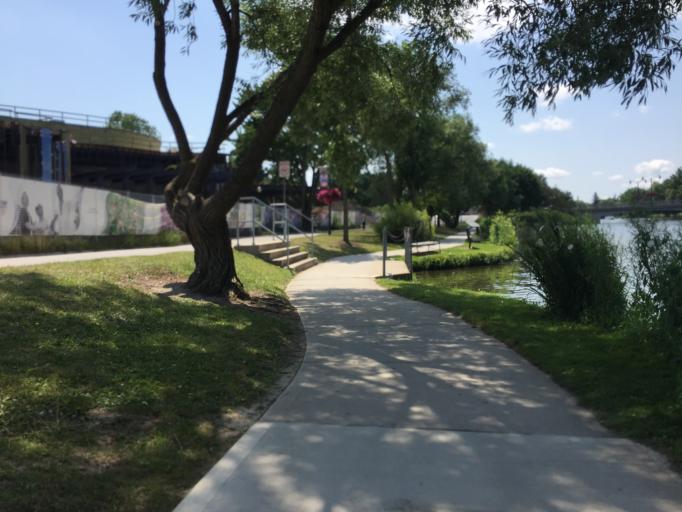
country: CA
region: Ontario
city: Stratford
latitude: 43.3741
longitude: -80.9776
